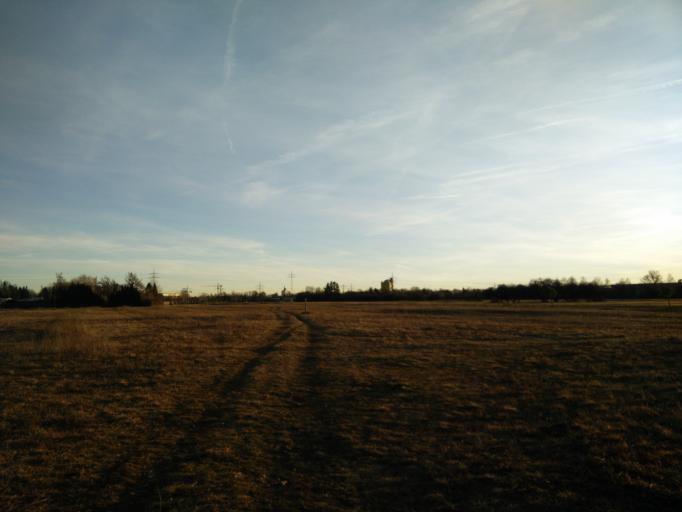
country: DE
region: Bavaria
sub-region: Upper Bavaria
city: Pasing
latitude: 48.1694
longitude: 11.4302
